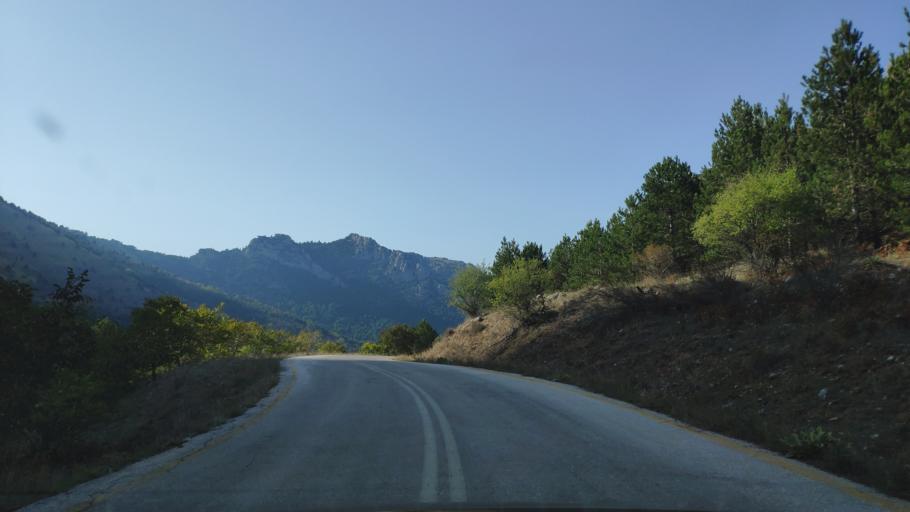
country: GR
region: West Greece
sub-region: Nomos Achaias
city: Aiyira
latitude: 38.0417
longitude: 22.3927
